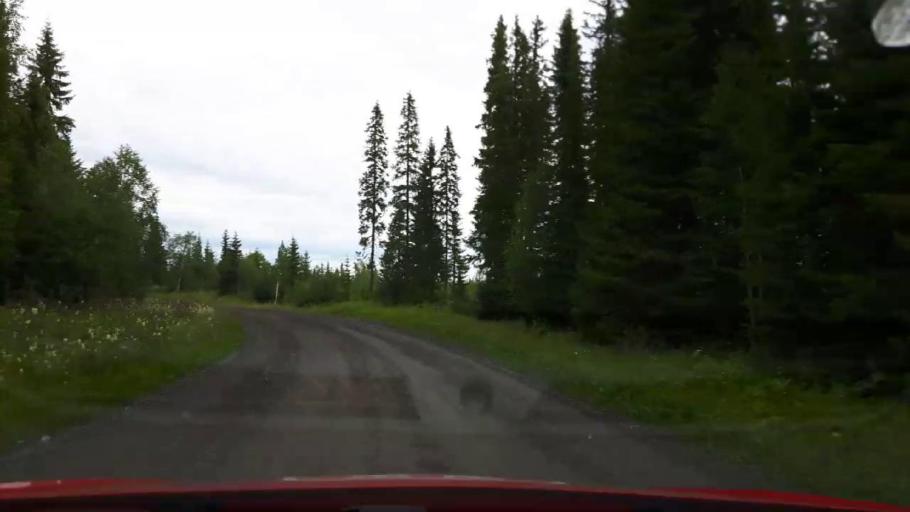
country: SE
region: Jaemtland
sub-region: OEstersunds Kommun
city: Lit
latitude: 63.4365
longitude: 15.2673
